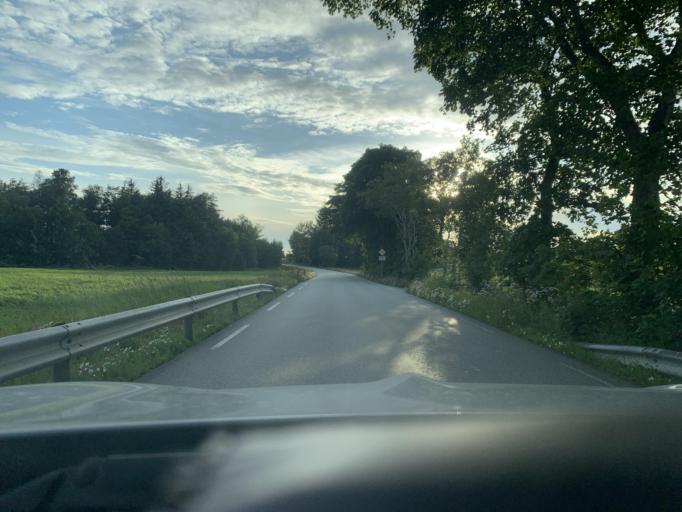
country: NO
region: Rogaland
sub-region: Ha
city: Naerbo
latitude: 58.6848
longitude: 5.7421
